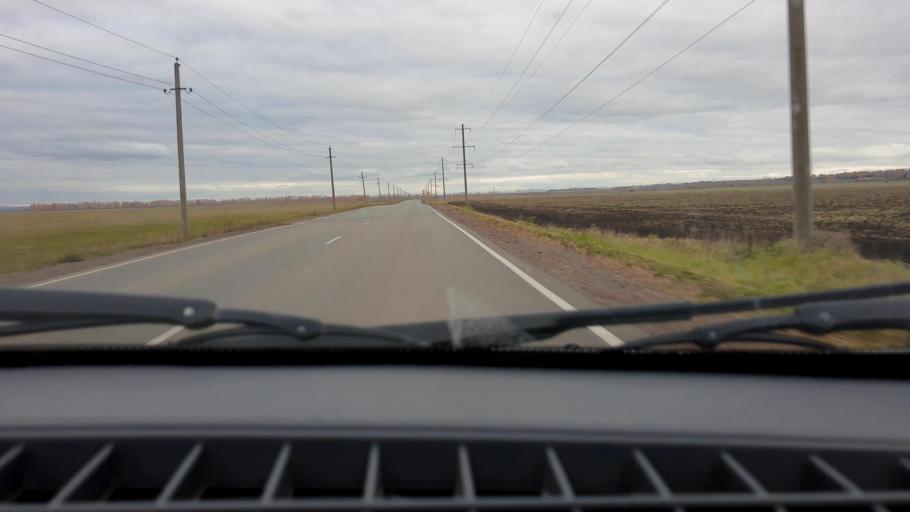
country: RU
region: Bashkortostan
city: Kabakovo
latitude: 54.5434
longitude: 56.0486
